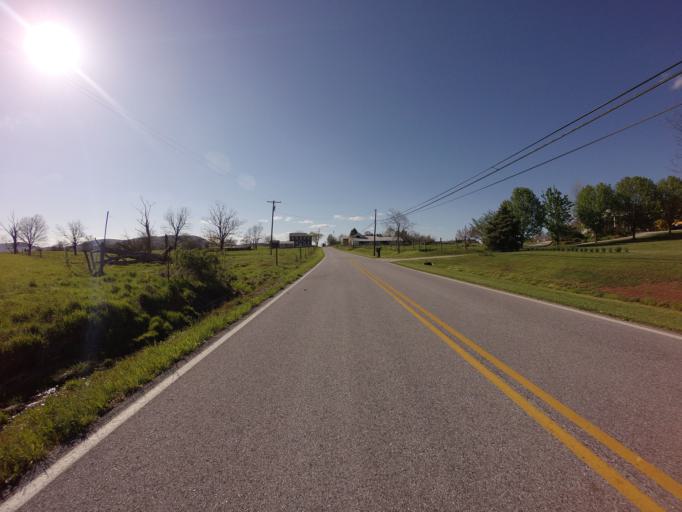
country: US
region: Maryland
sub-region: Frederick County
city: Emmitsburg
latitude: 39.6804
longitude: -77.3132
